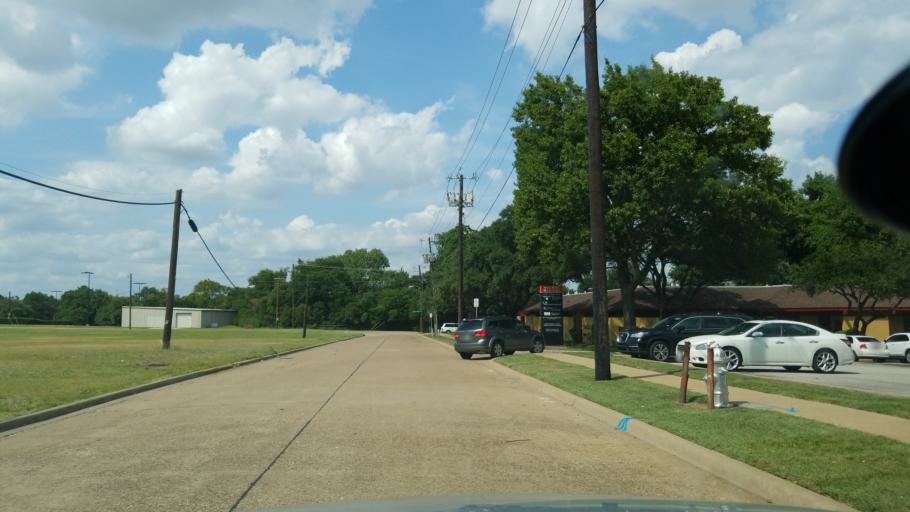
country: US
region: Texas
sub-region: Dallas County
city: Garland
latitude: 32.9174
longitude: -96.6589
